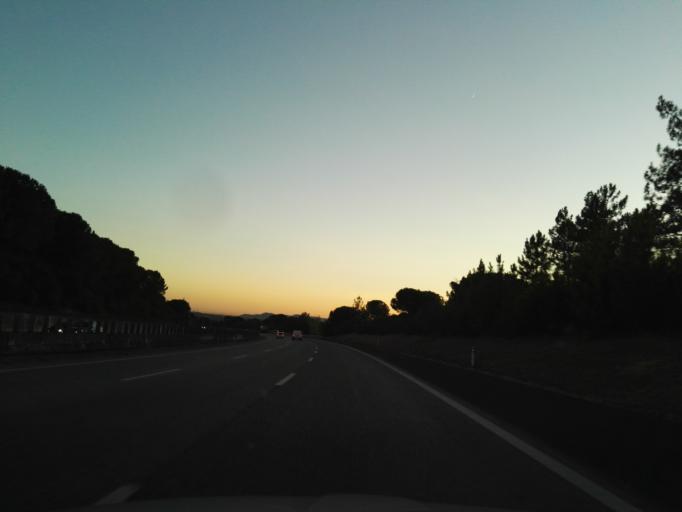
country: PT
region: Lisbon
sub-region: Azambuja
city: Aveiras de Cima
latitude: 39.1088
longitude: -8.9331
